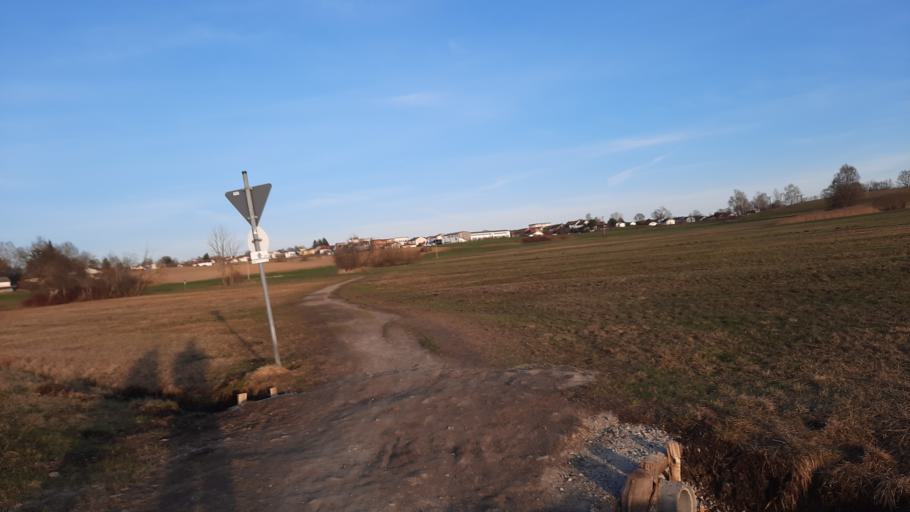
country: DE
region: Bavaria
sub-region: Upper Bavaria
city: Ebersberg
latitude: 48.0782
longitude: 11.9443
